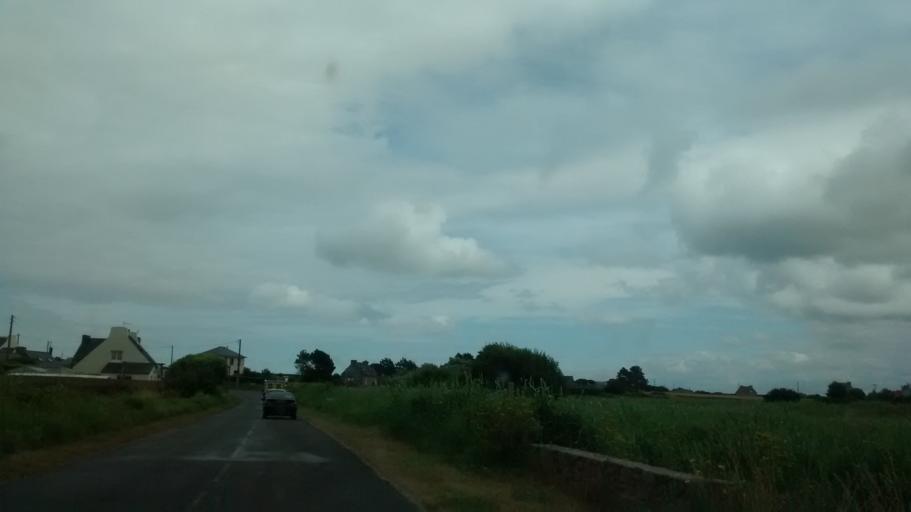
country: FR
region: Brittany
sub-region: Departement du Finistere
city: Guisseny
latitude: 48.6347
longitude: -4.4328
